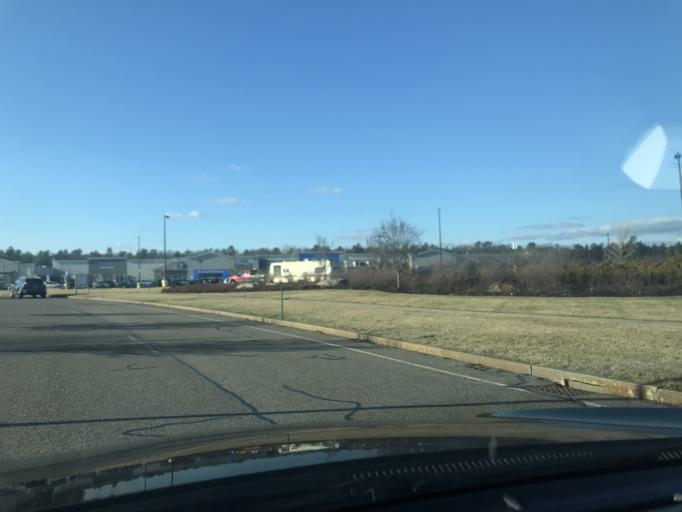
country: US
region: Massachusetts
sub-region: Plymouth County
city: North Plymouth
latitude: 41.9541
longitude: -70.7158
